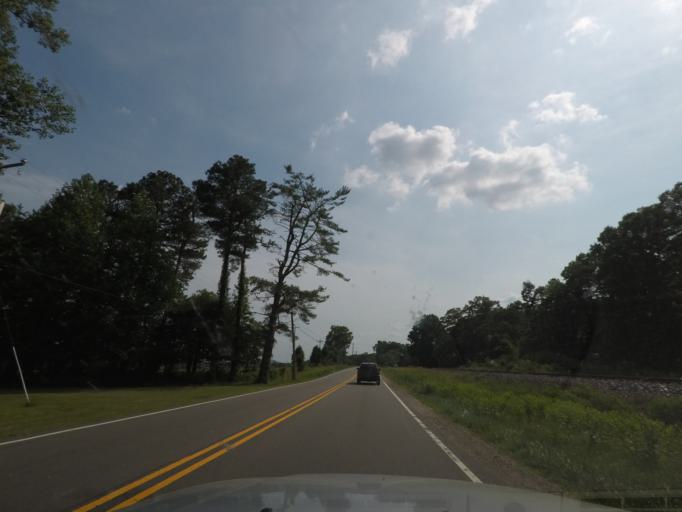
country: US
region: Virginia
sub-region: Buckingham County
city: Buckingham
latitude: 37.5473
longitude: -78.4448
